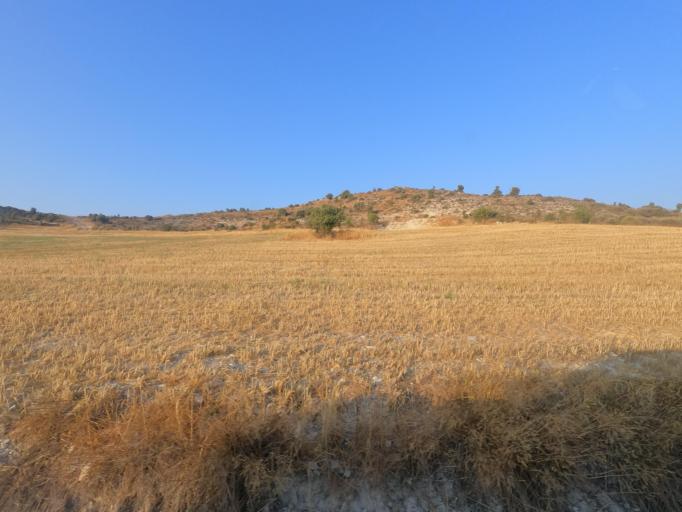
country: CY
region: Larnaka
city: Psevdas
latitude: 34.9035
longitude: 33.5060
